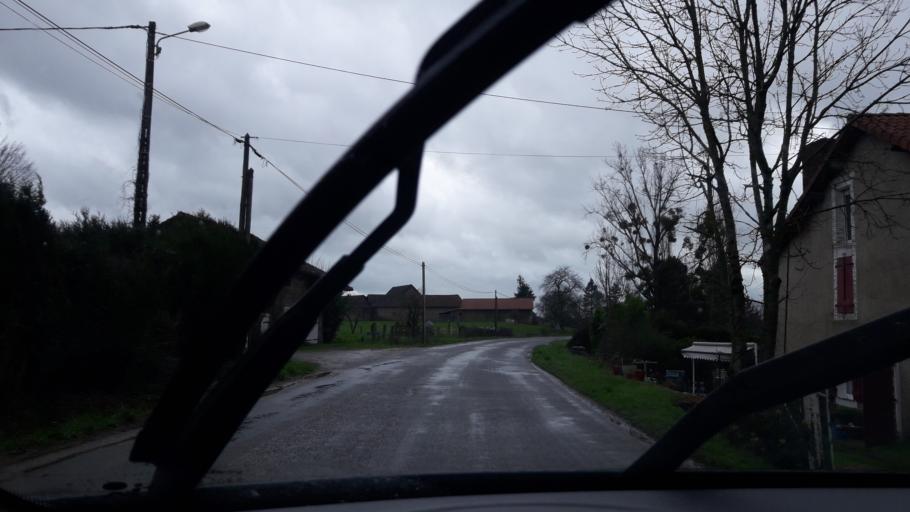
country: FR
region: Limousin
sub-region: Departement de la Haute-Vienne
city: Saint-Paul
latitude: 45.7464
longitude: 1.4050
